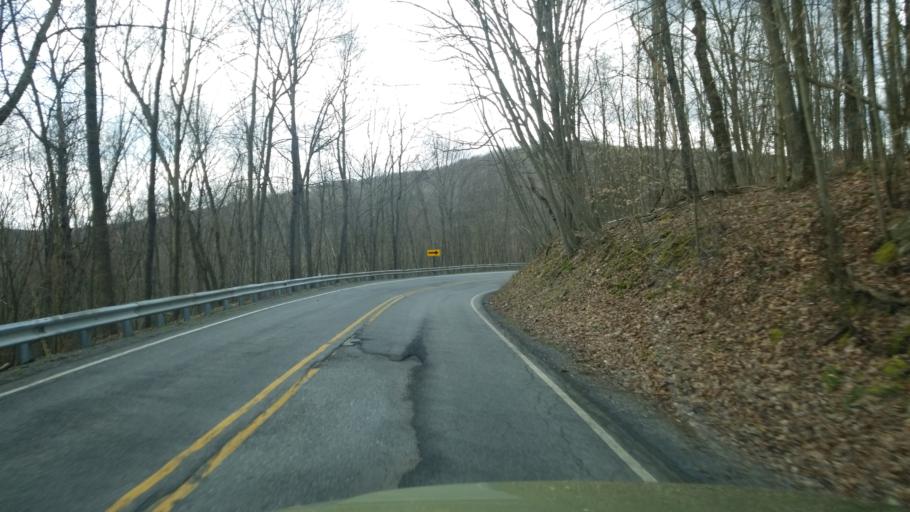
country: US
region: Pennsylvania
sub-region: Clearfield County
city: Curwensville
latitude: 40.8866
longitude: -78.4585
